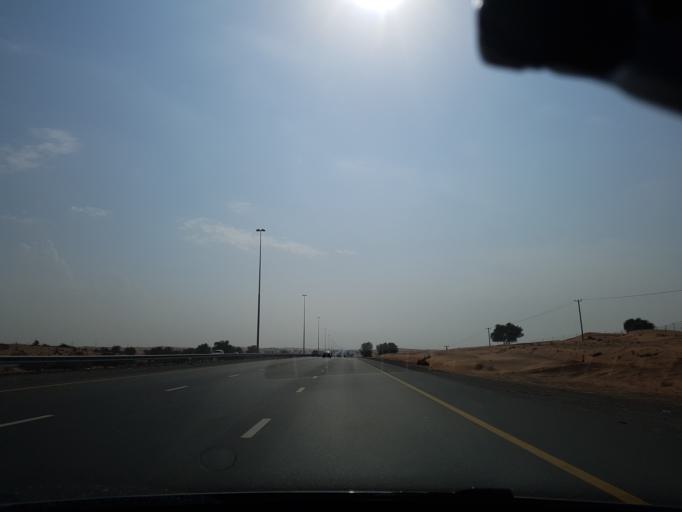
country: AE
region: Umm al Qaywayn
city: Umm al Qaywayn
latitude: 25.5196
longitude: 55.7136
